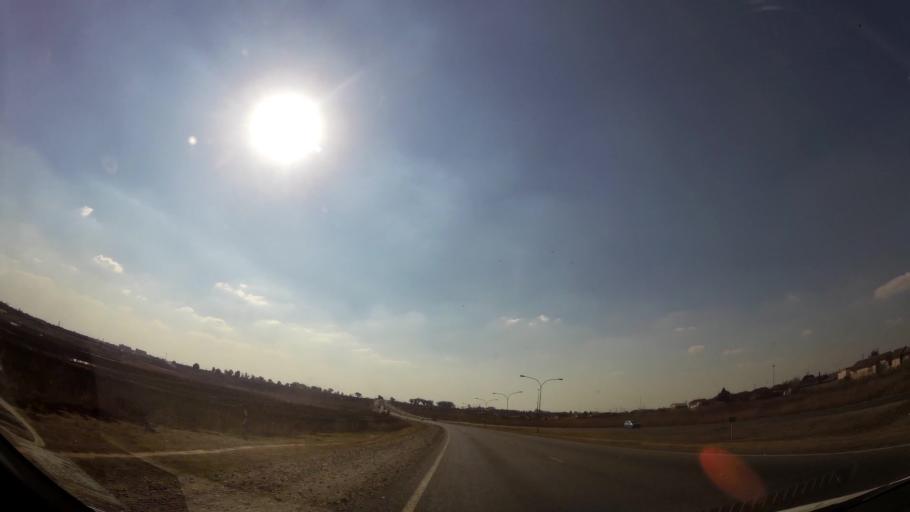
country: ZA
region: Gauteng
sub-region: Ekurhuleni Metropolitan Municipality
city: Benoni
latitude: -26.2312
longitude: 28.3219
